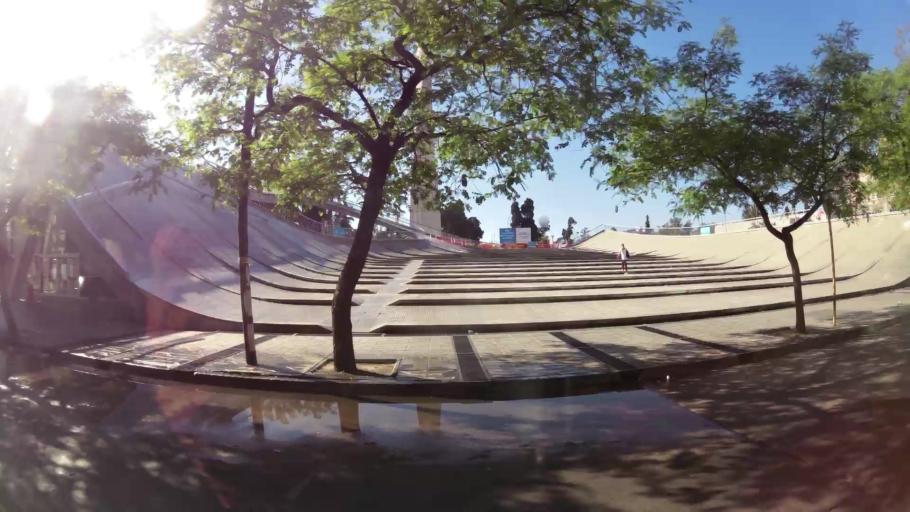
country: AR
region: Cordoba
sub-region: Departamento de Capital
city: Cordoba
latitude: -31.4277
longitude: -64.1826
